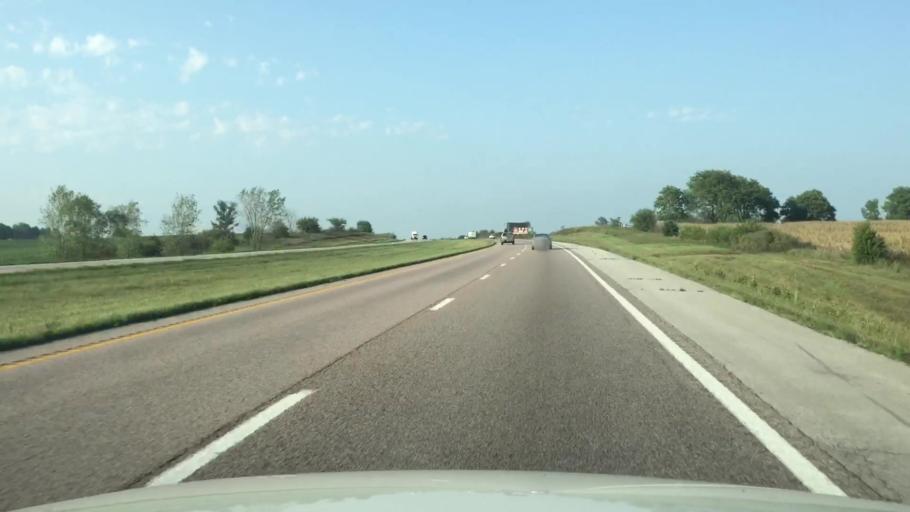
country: US
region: Missouri
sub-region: Clinton County
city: Lathrop
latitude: 39.5190
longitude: -94.2832
